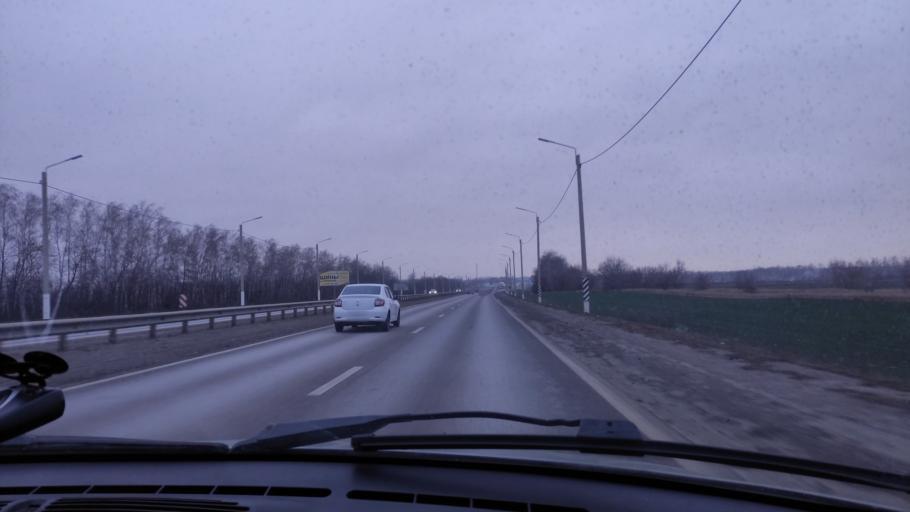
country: RU
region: Tambov
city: Komsomolets
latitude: 52.7262
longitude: 41.3440
